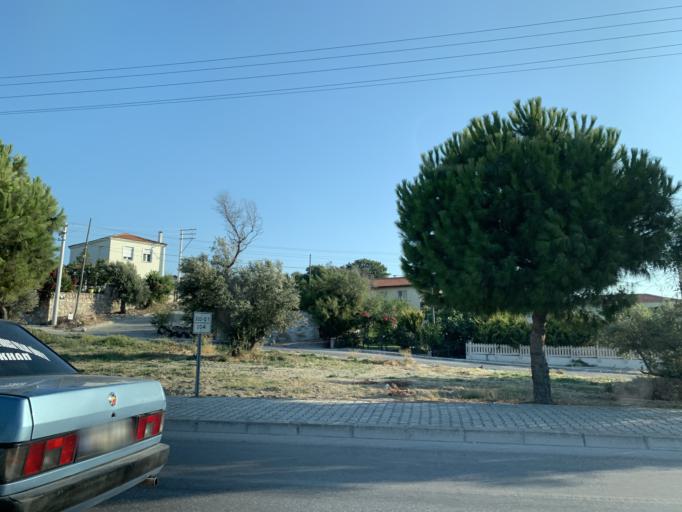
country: TR
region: Izmir
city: Alacati
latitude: 38.3091
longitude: 26.3515
